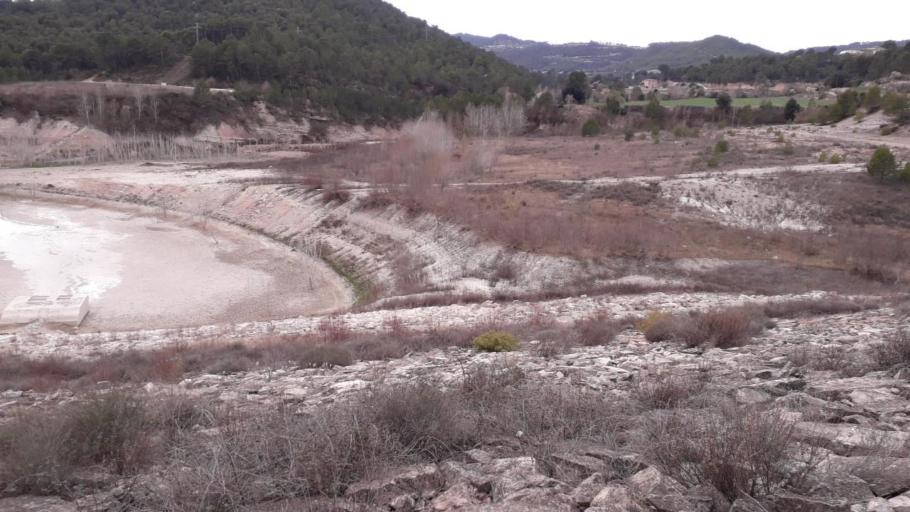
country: ES
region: Catalonia
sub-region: Provincia de Barcelona
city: Sant Marti de Tous
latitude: 41.5567
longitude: 1.4933
